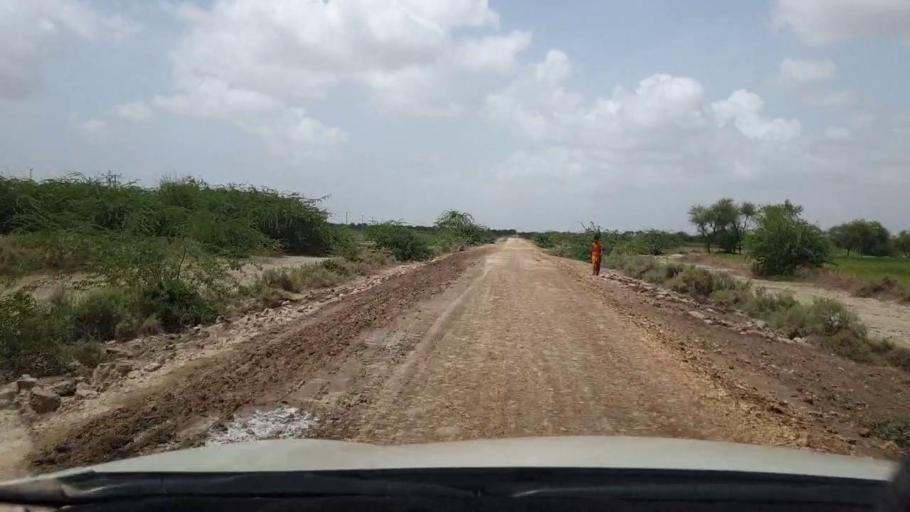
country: PK
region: Sindh
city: Kadhan
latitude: 24.3756
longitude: 68.8585
